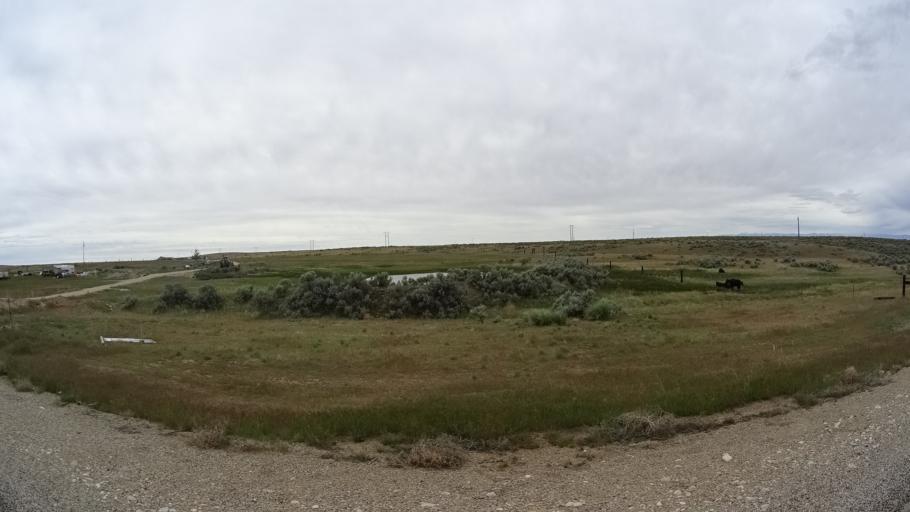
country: US
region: Idaho
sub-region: Ada County
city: Boise
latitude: 43.4686
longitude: -116.0721
